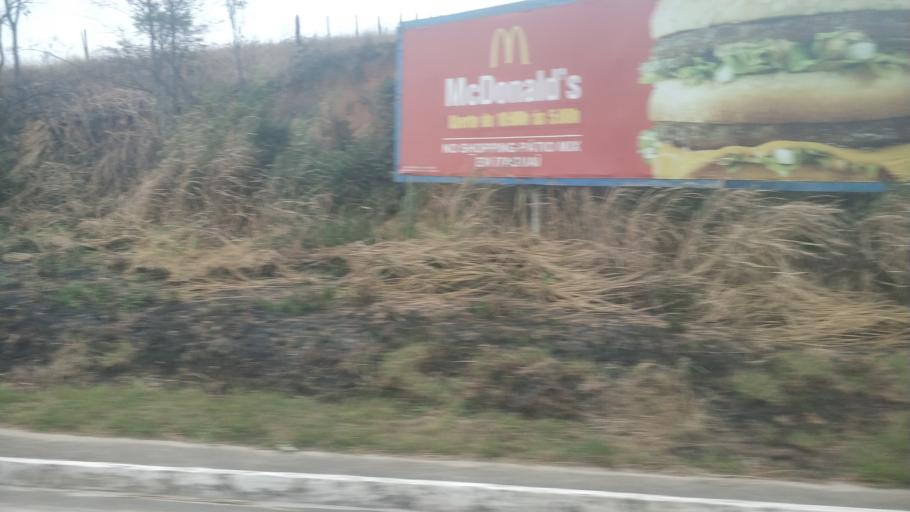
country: BR
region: Rio de Janeiro
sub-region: Seropedica
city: Seropedica
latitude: -22.7822
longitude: -43.6588
